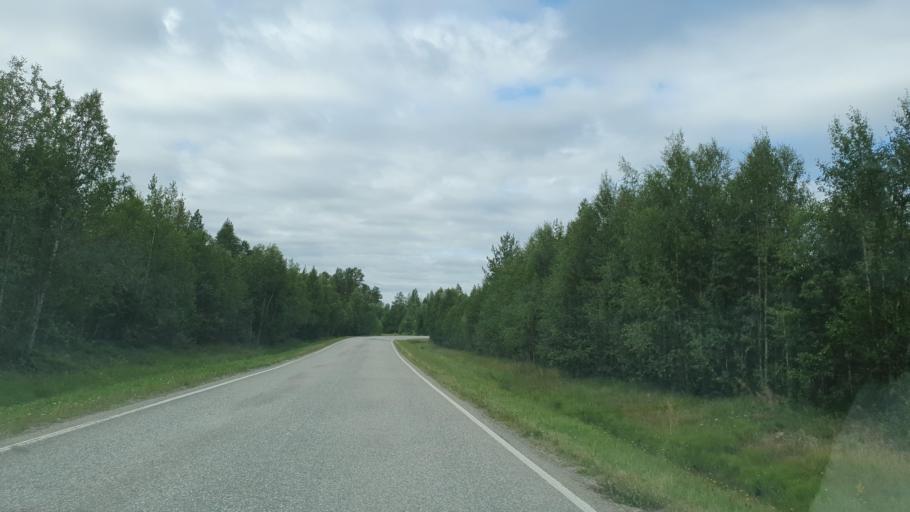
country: FI
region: Lapland
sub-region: Tunturi-Lappi
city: Kittilae
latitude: 67.6114
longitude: 25.2138
